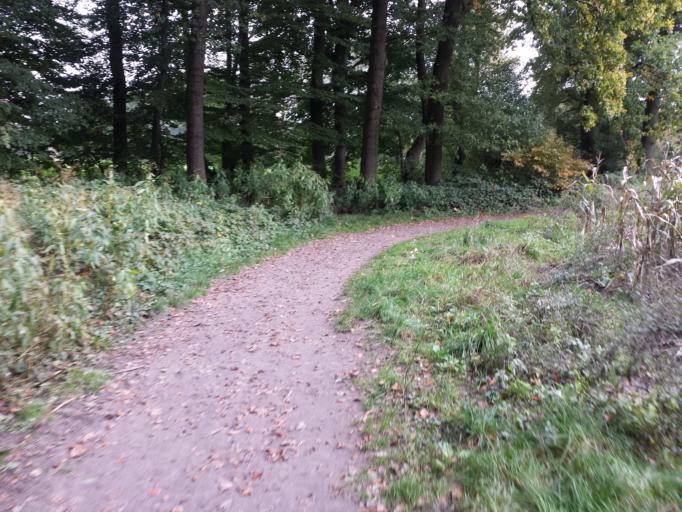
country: DE
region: North Rhine-Westphalia
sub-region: Regierungsbezirk Detmold
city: Guetersloh
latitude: 51.9220
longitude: 8.3603
